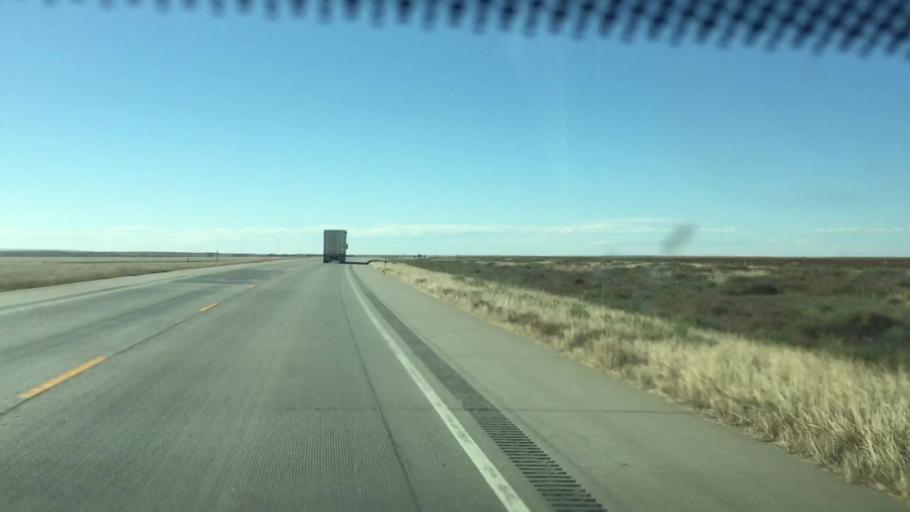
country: US
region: Colorado
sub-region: Kiowa County
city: Eads
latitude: 38.7888
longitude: -102.9297
